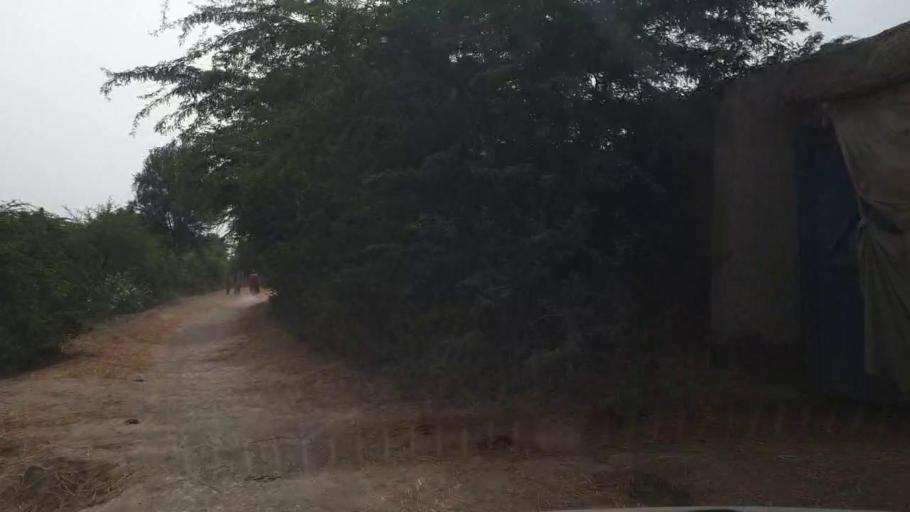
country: PK
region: Sindh
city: Matli
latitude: 24.9865
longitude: 68.7022
